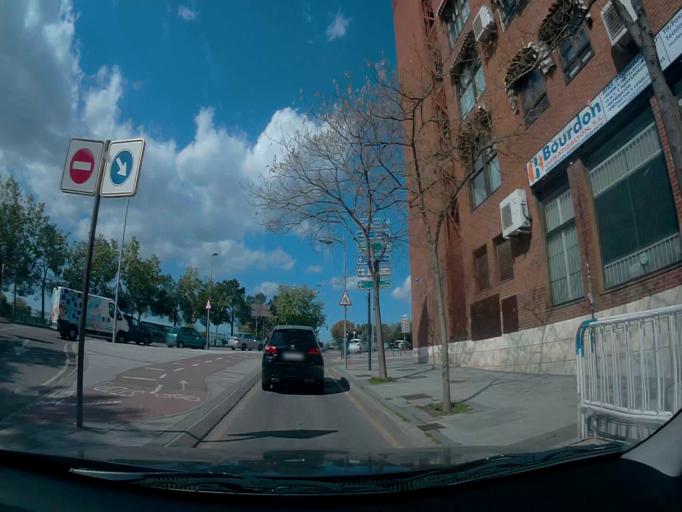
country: ES
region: Madrid
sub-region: Provincia de Madrid
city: Alcorcon
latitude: 40.3515
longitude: -3.8293
